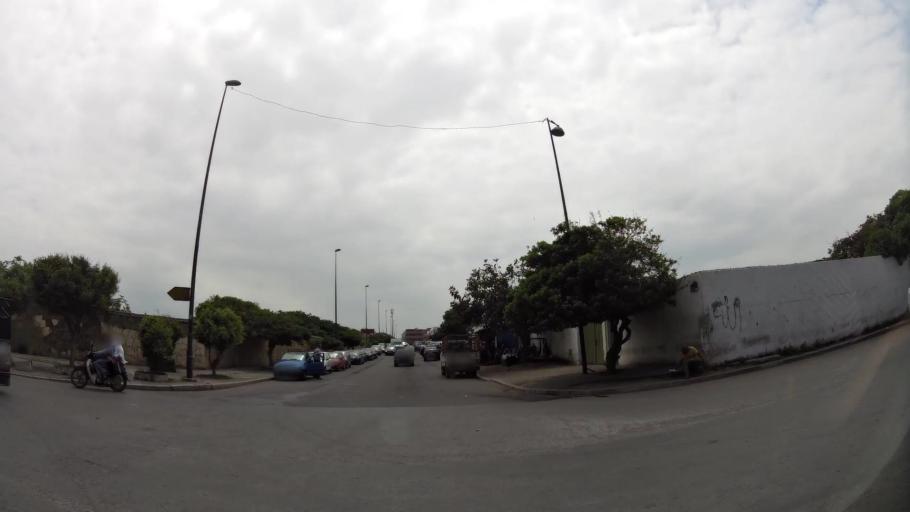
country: MA
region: Rabat-Sale-Zemmour-Zaer
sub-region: Skhirate-Temara
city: Temara
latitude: 33.9831
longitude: -6.8893
